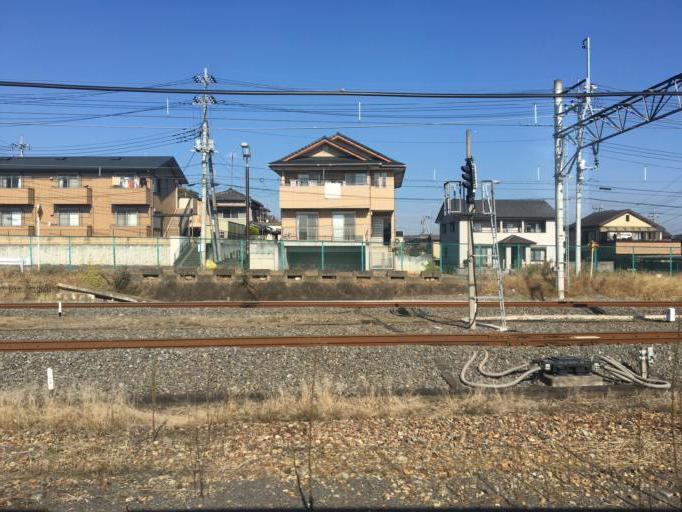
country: JP
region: Tochigi
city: Sano
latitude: 36.3168
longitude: 139.5803
